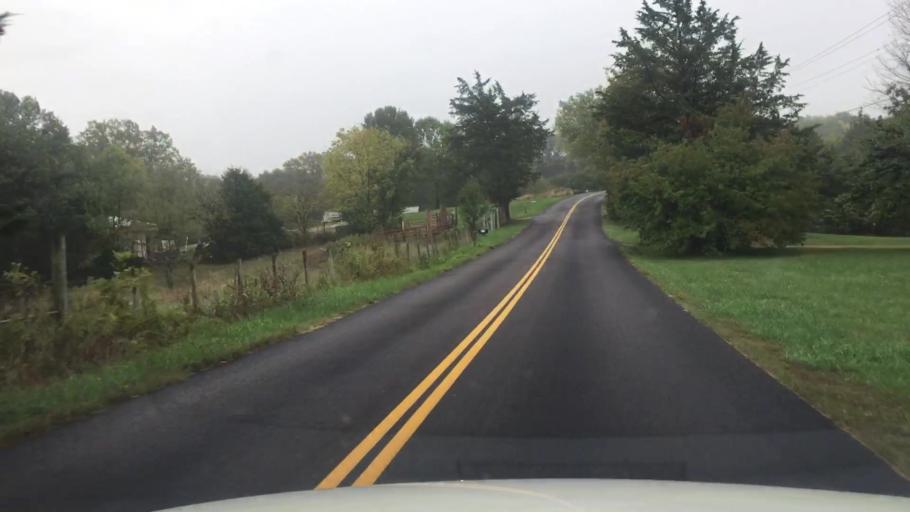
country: US
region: Missouri
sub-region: Boone County
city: Columbia
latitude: 38.8615
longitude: -92.3383
